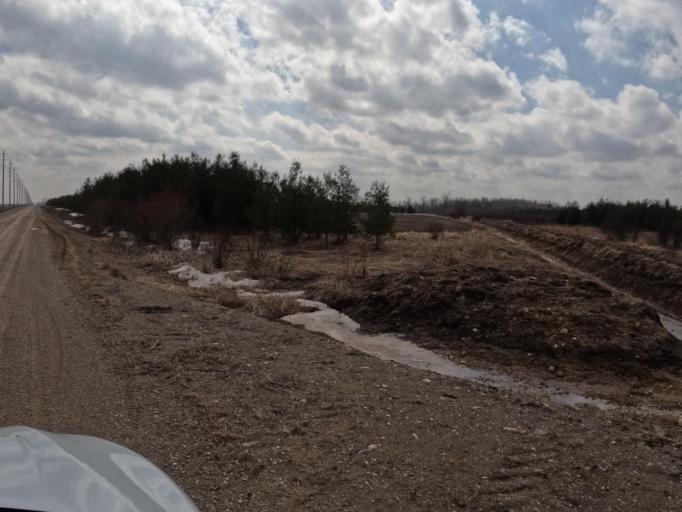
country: CA
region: Ontario
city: Shelburne
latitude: 44.0503
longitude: -80.3198
